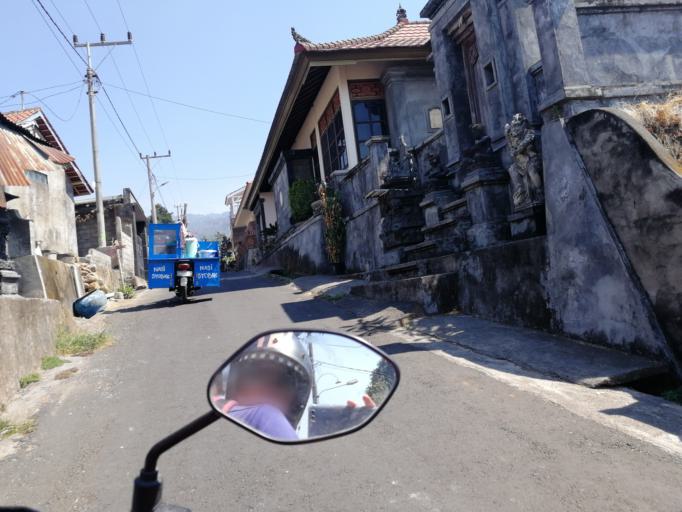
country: ID
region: Bali
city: Banjar Kedisan
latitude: -8.1515
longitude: 115.3078
